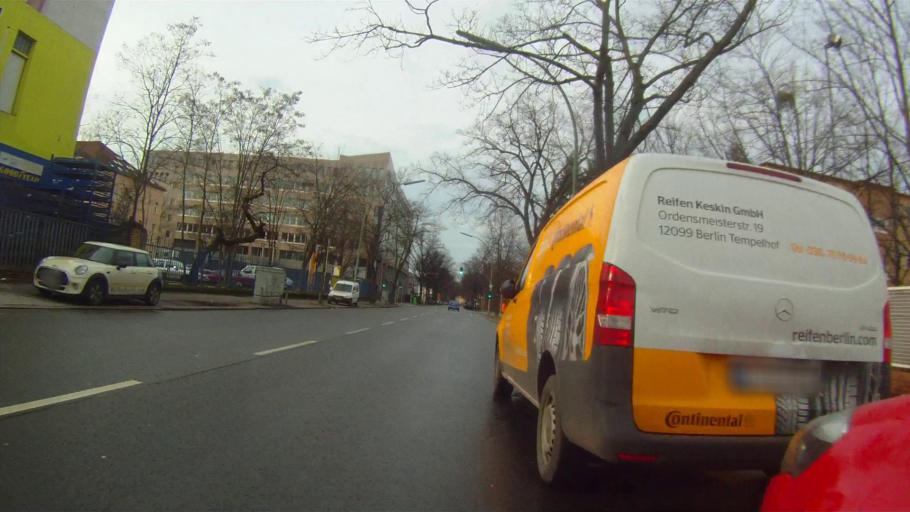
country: DE
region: Berlin
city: Tempelhof Bezirk
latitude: 52.4583
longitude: 13.3945
